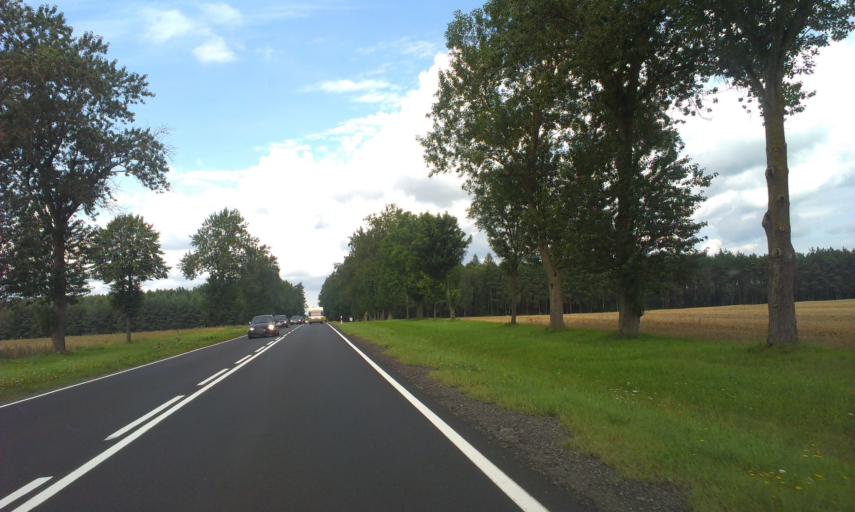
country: PL
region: West Pomeranian Voivodeship
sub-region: Powiat koszalinski
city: Bobolice
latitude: 54.0538
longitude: 16.4249
